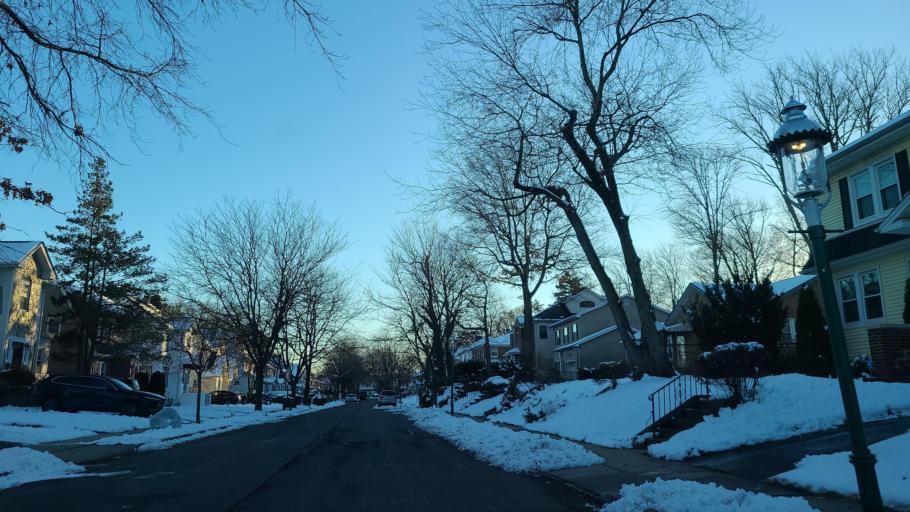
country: US
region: New Jersey
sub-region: Essex County
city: Irvington
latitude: 40.7486
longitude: -74.2365
